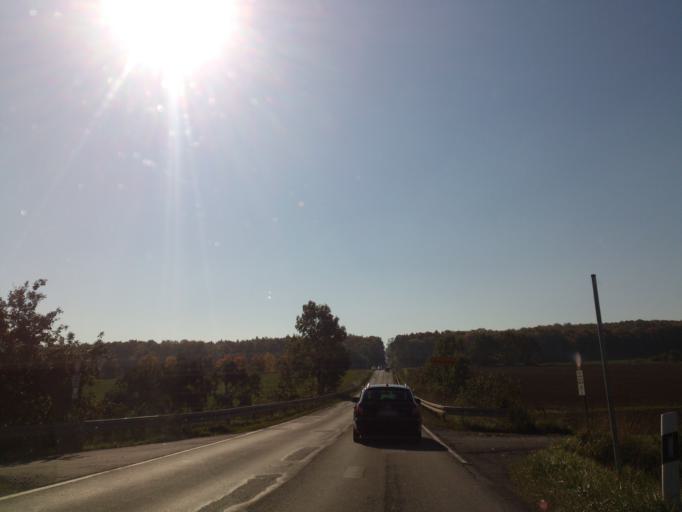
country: DE
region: Hesse
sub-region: Regierungsbezirk Kassel
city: Calden
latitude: 51.3571
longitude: 9.4165
